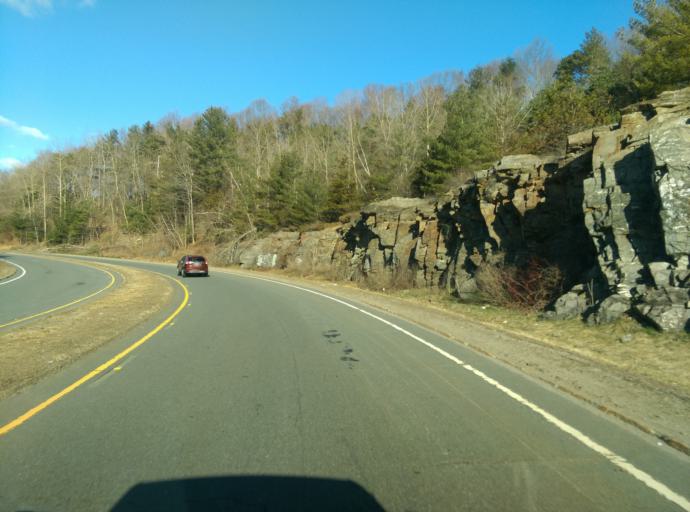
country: US
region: Massachusetts
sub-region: Essex County
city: Haverhill
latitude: 42.8042
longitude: -71.0520
